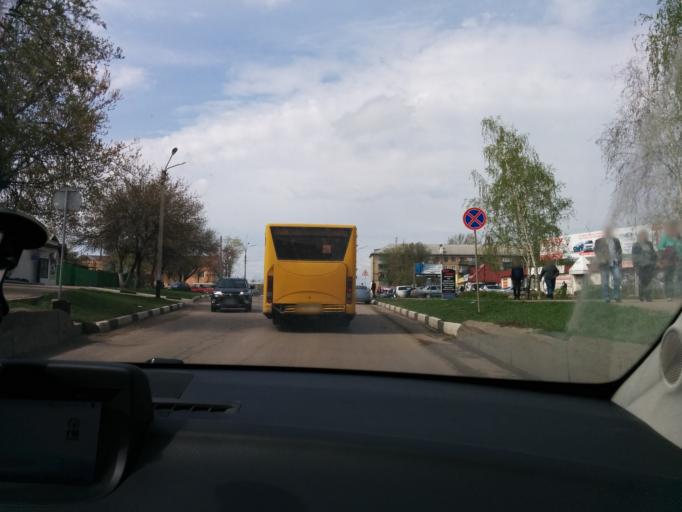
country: RU
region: Tambov
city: Tambov
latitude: 52.7201
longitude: 41.4260
